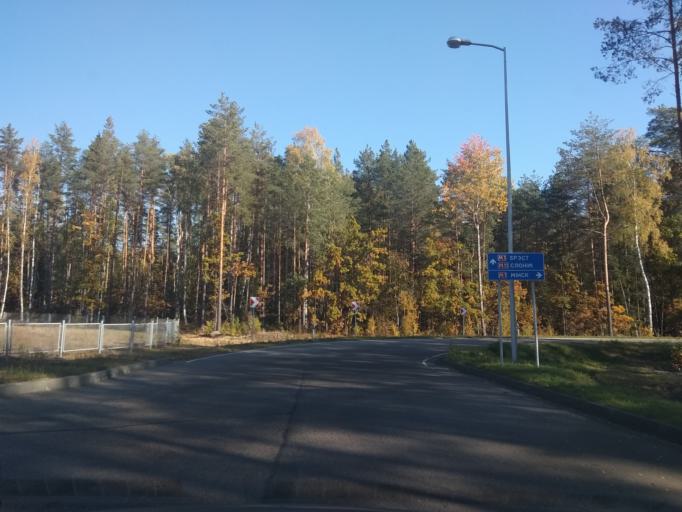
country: BY
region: Grodnenskaya
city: Zhyrovichy
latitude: 52.8584
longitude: 25.6514
